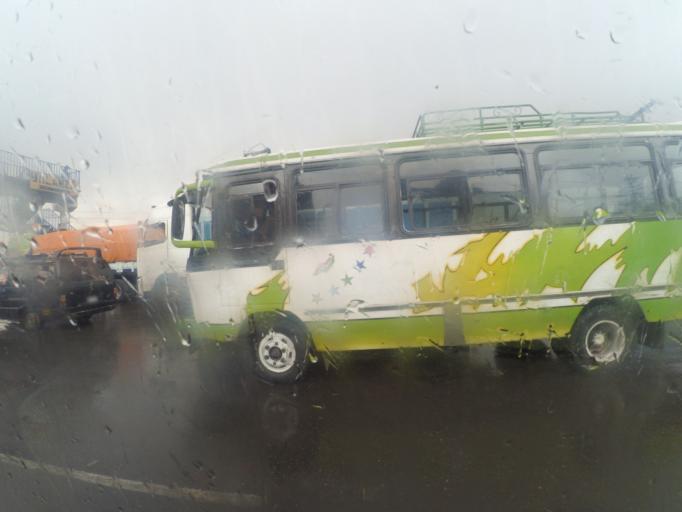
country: BO
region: La Paz
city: La Paz
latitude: -16.5229
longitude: -68.1692
